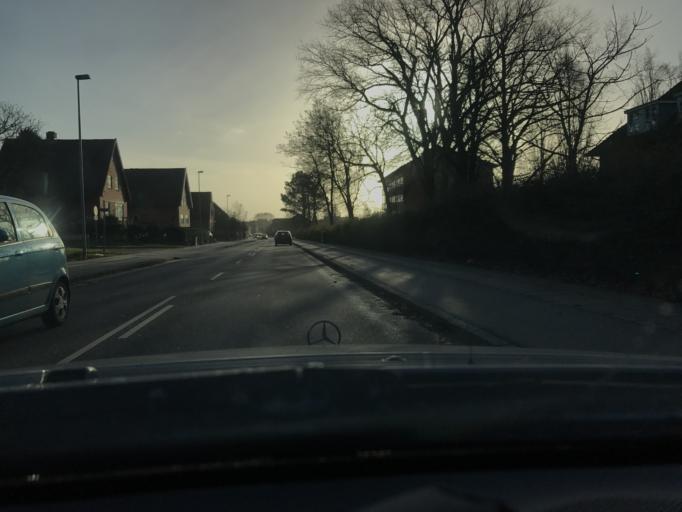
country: DK
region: South Denmark
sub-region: Sonderborg Kommune
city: Sonderborg
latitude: 54.9180
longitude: 9.7867
